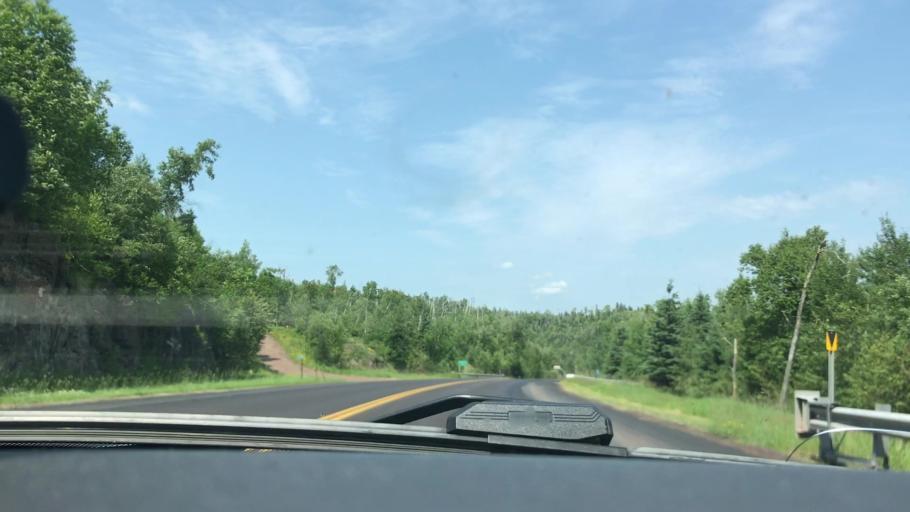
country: US
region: Minnesota
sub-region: Lake County
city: Silver Bay
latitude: 47.3719
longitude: -91.1656
